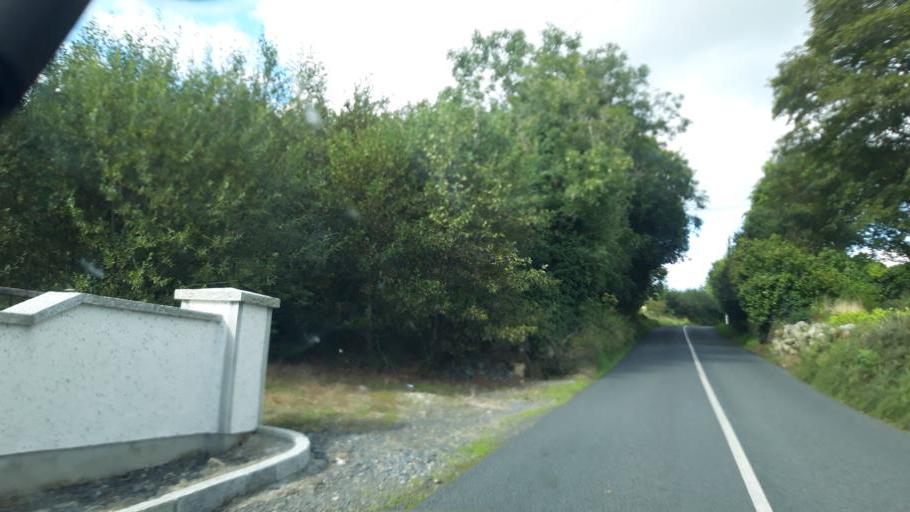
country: GB
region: Northern Ireland
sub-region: Down District
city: Warrenpoint
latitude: 54.0239
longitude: -6.2902
